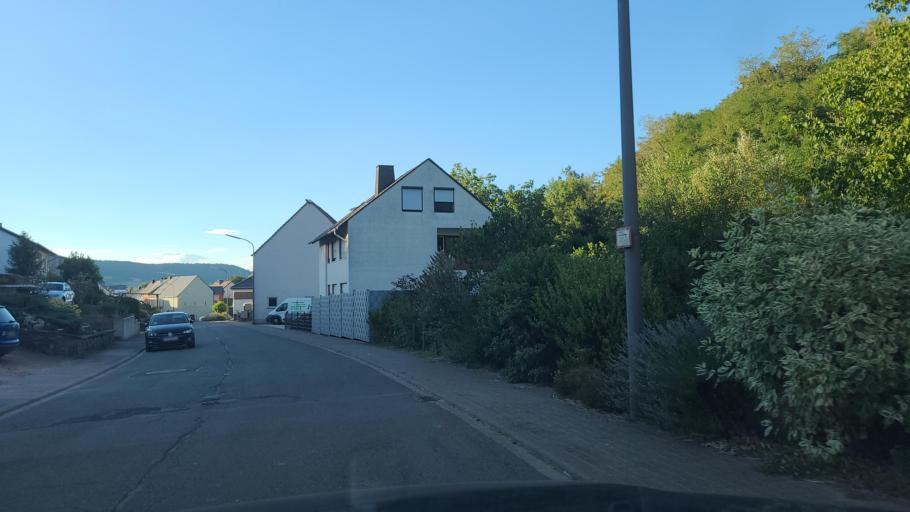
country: DE
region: Rheinland-Pfalz
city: Hetzerath
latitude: 49.8719
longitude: 6.8184
